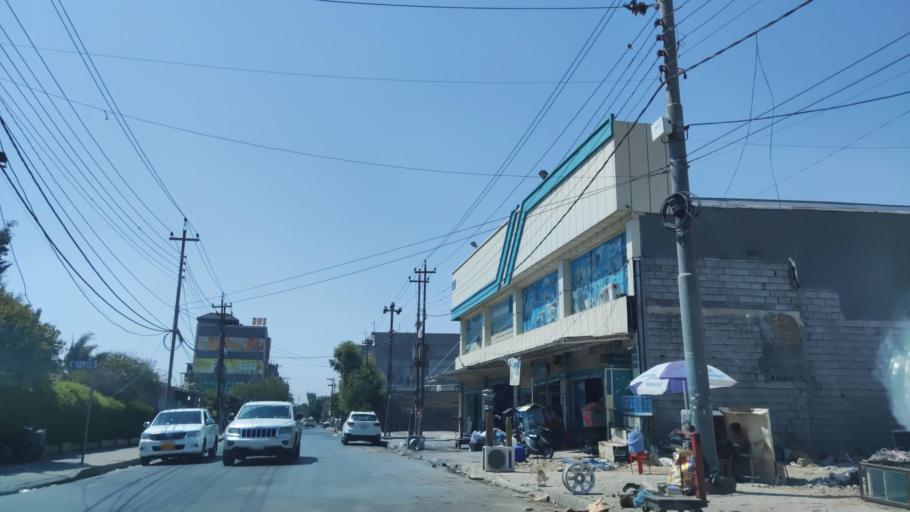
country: IQ
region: Arbil
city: Erbil
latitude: 36.1878
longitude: 44.0246
